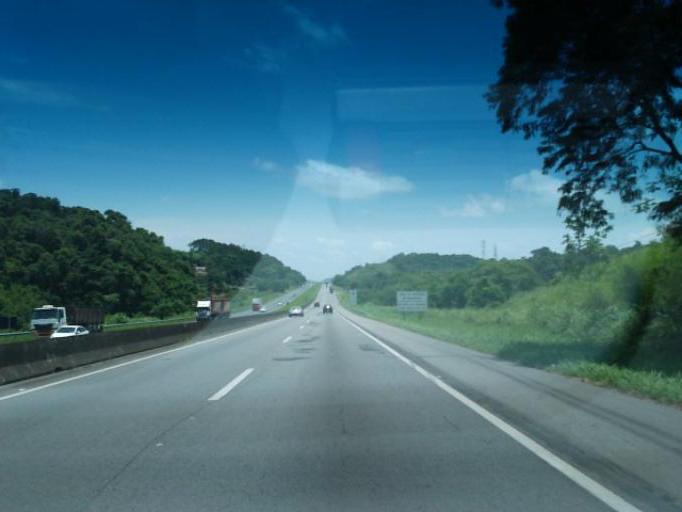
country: BR
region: Sao Paulo
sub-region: Juquia
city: Juquia
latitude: -24.3339
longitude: -47.5989
